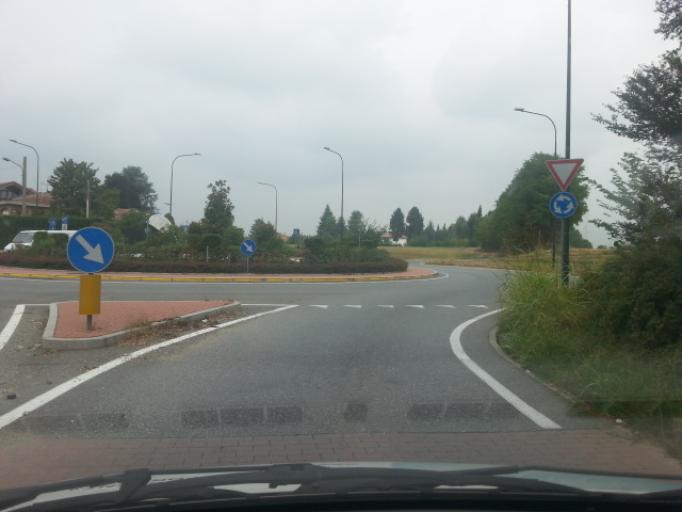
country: IT
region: Piedmont
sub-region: Provincia di Torino
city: Rivalta di Torino
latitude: 45.0394
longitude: 7.5231
